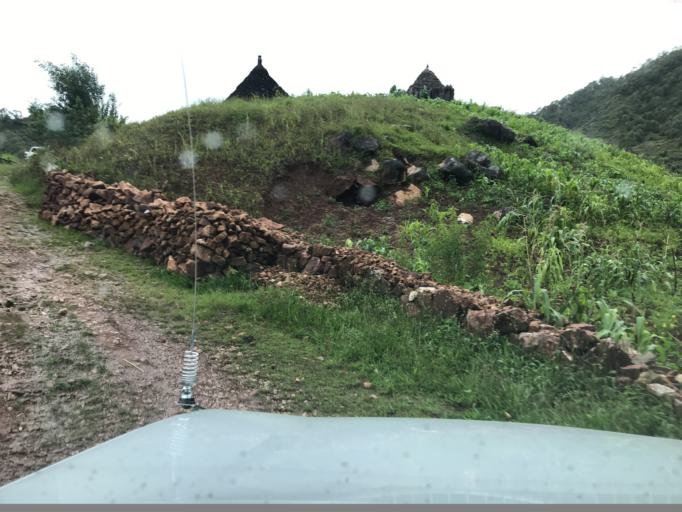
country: TL
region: Ainaro
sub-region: Ainaro
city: Ainaro
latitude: -8.8675
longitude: 125.5520
